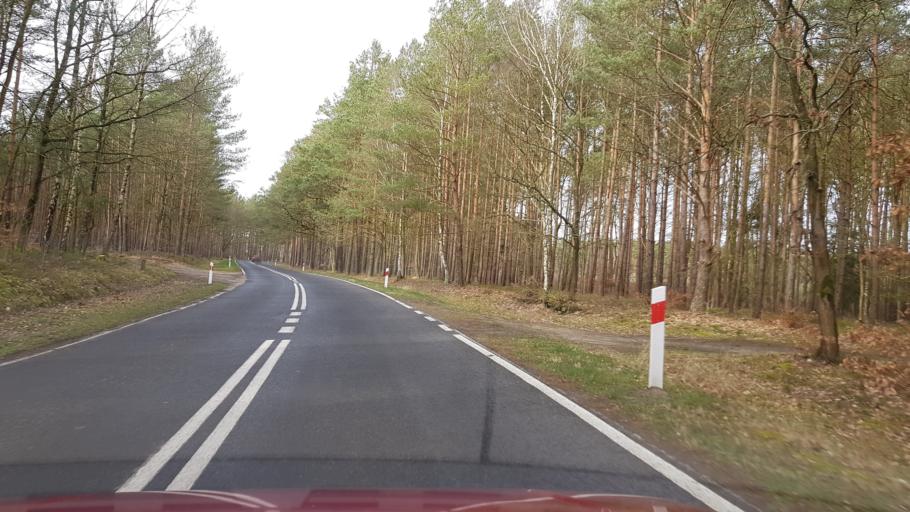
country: PL
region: West Pomeranian Voivodeship
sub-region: Powiat policki
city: Nowe Warpno
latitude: 53.6777
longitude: 14.3624
